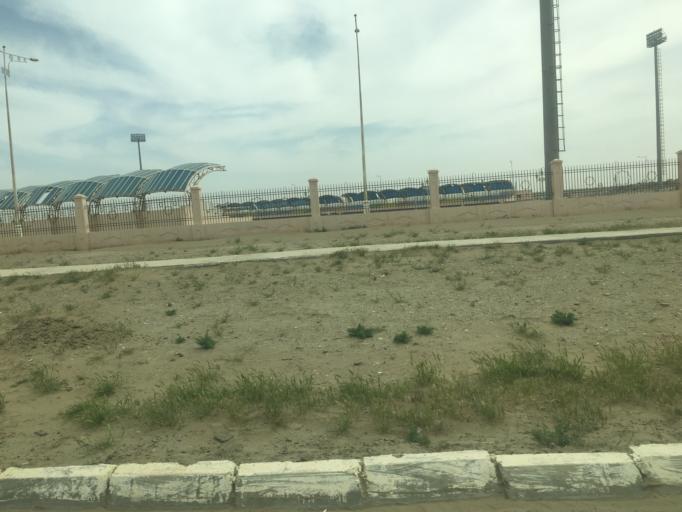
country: TM
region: Balkan
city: Turkmenbasy
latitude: 39.4080
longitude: 53.1366
